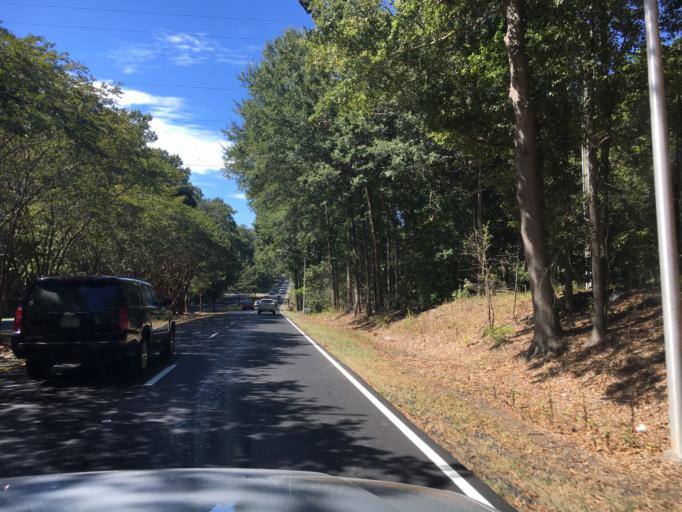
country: US
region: South Carolina
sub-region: Spartanburg County
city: Saxon
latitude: 34.9390
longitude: -81.9641
